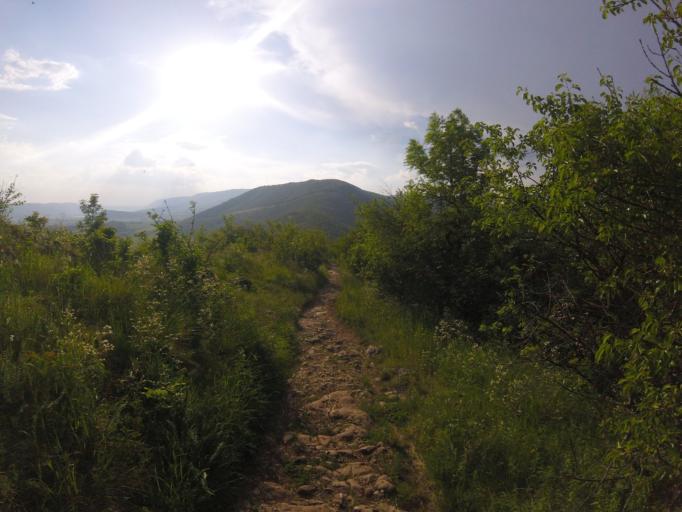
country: SK
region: Kosicky
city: Medzev
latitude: 48.6117
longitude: 20.8729
